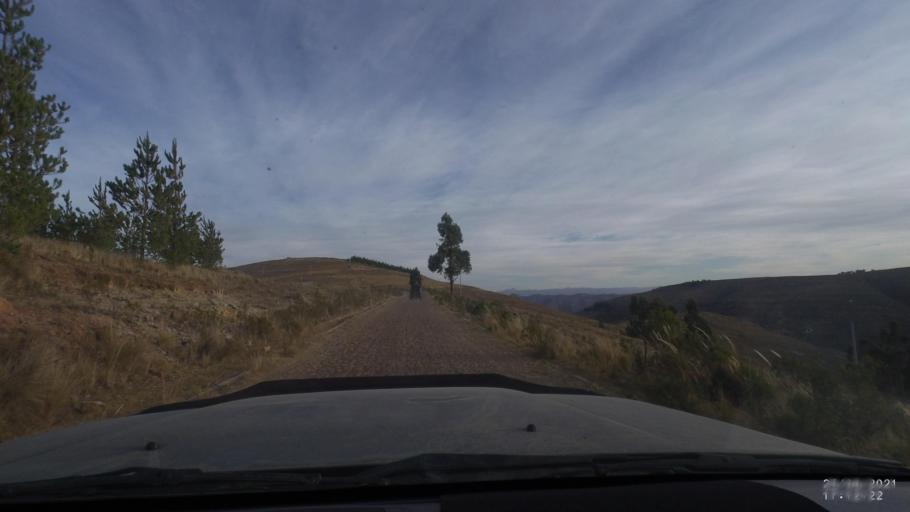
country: BO
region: Cochabamba
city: Arani
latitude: -17.8505
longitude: -65.7007
